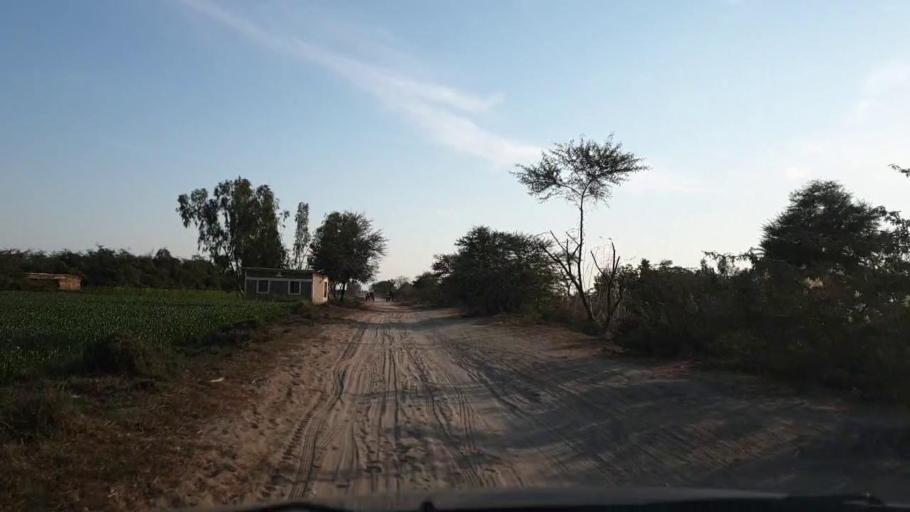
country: PK
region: Sindh
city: Khadro
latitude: 26.2245
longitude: 68.7397
